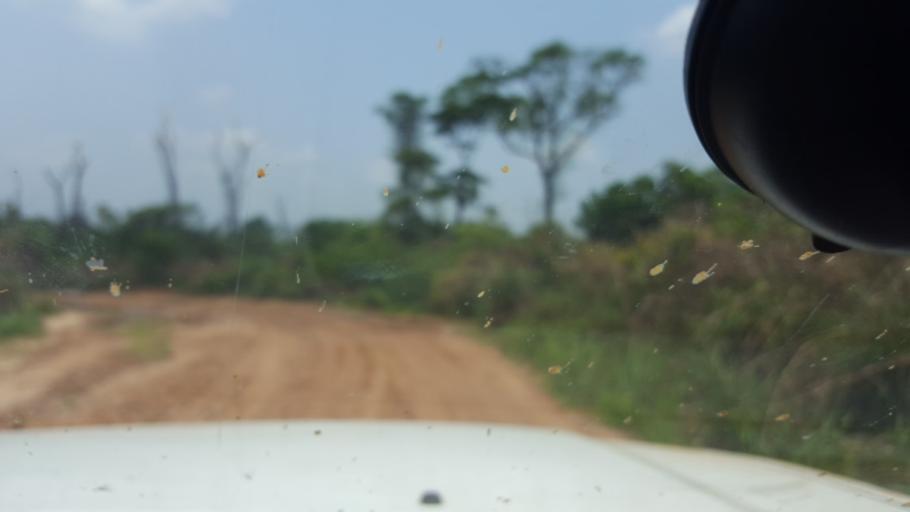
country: CD
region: Bandundu
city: Mushie
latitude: -3.7509
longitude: 16.6369
